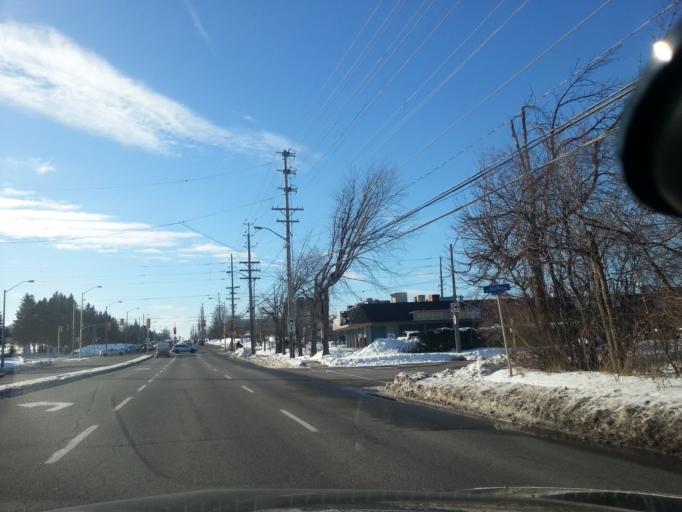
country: CA
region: Ontario
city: Ottawa
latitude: 45.3895
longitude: -75.6162
